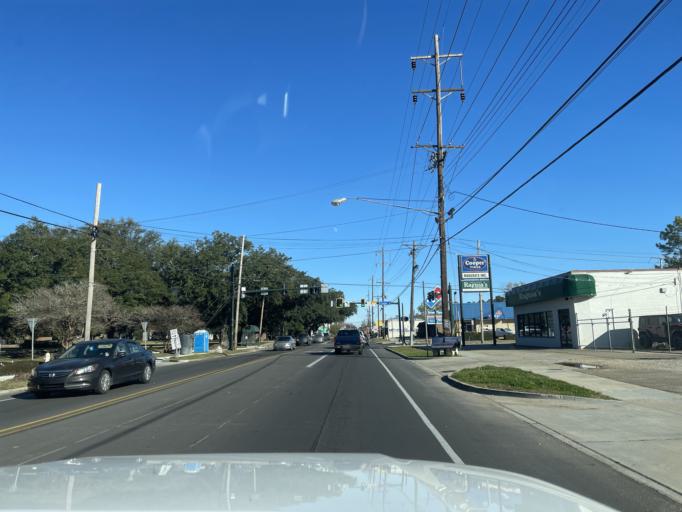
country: US
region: Louisiana
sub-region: East Baton Rouge Parish
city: Baton Rouge
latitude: 30.4441
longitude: -91.1605
